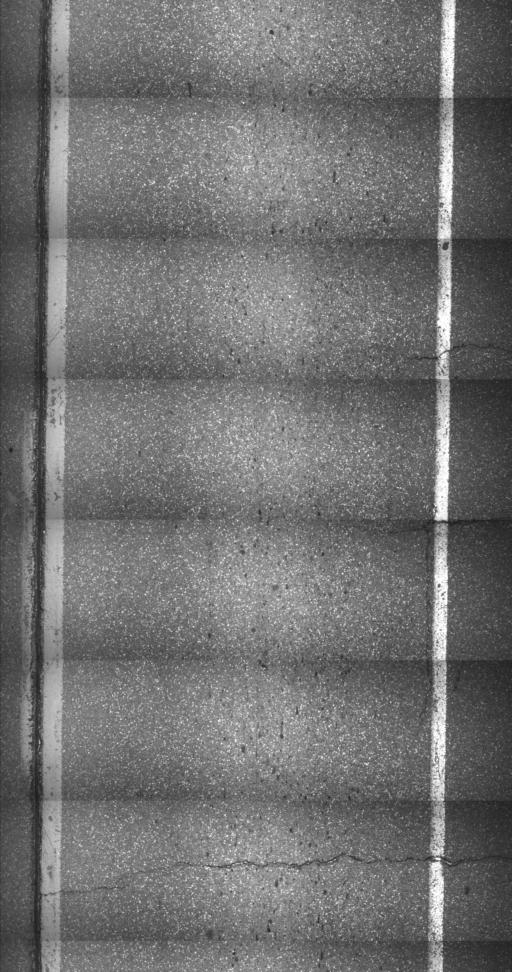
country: US
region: Vermont
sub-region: Orleans County
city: Newport
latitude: 44.8542
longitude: -72.2645
